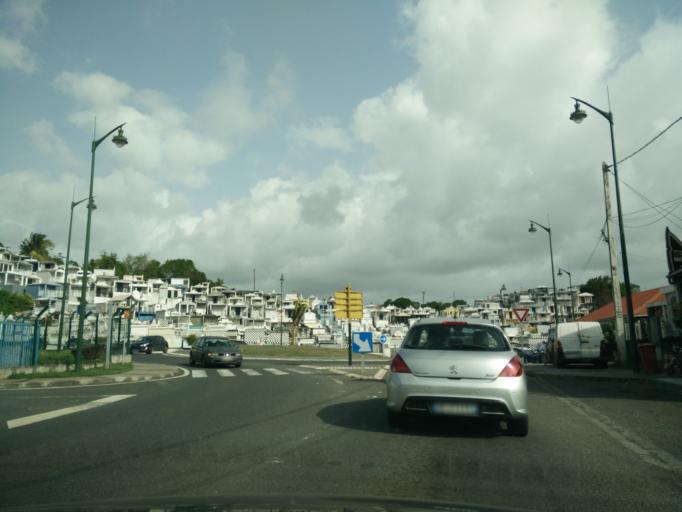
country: GP
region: Guadeloupe
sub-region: Guadeloupe
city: Petit-Canal
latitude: 16.3303
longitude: -61.4606
